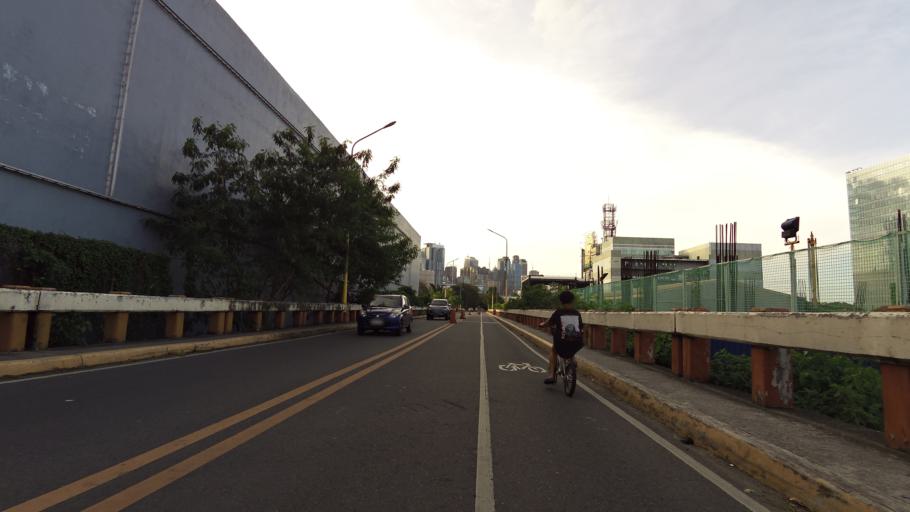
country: PH
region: Metro Manila
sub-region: Pasig
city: Pasig City
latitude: 14.5760
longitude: 121.0752
